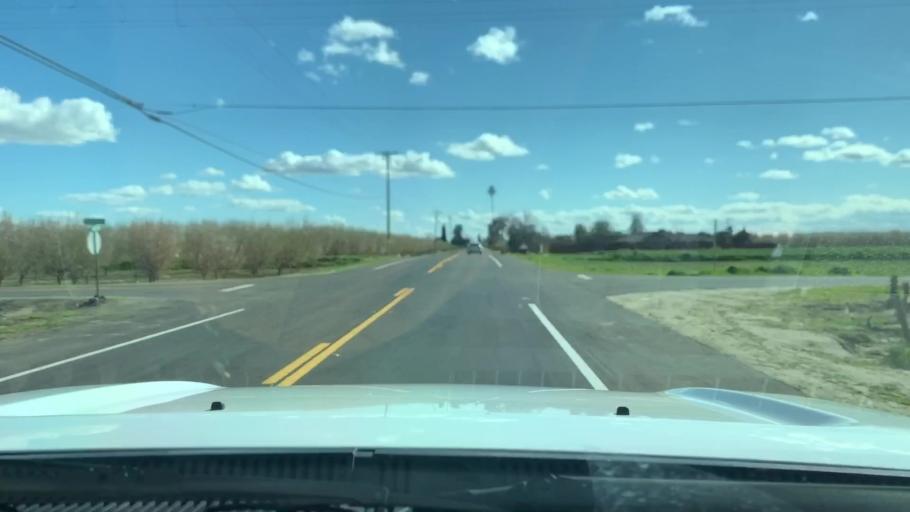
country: US
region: California
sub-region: Fresno County
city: Fowler
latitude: 36.5911
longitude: -119.6825
